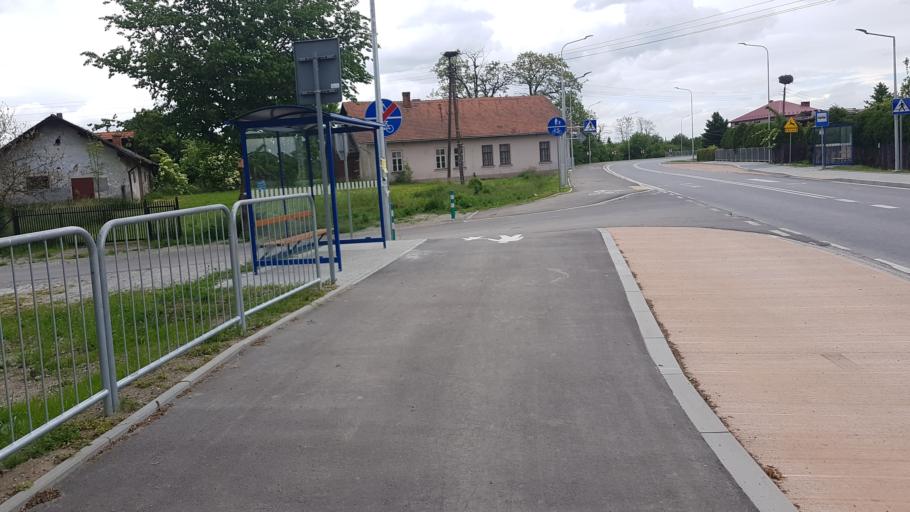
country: PL
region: Lesser Poland Voivodeship
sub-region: Powiat proszowicki
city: Nowe Brzesko
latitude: 50.1134
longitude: 20.3786
